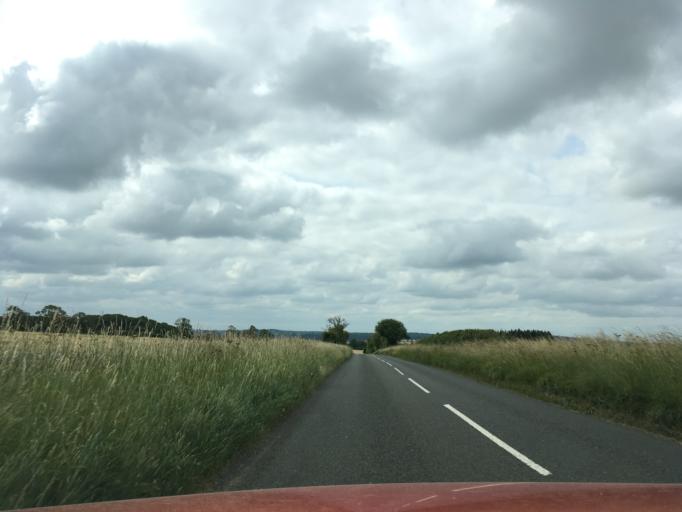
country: GB
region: England
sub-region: Oxfordshire
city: Charlbury
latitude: 51.9073
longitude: -1.4886
